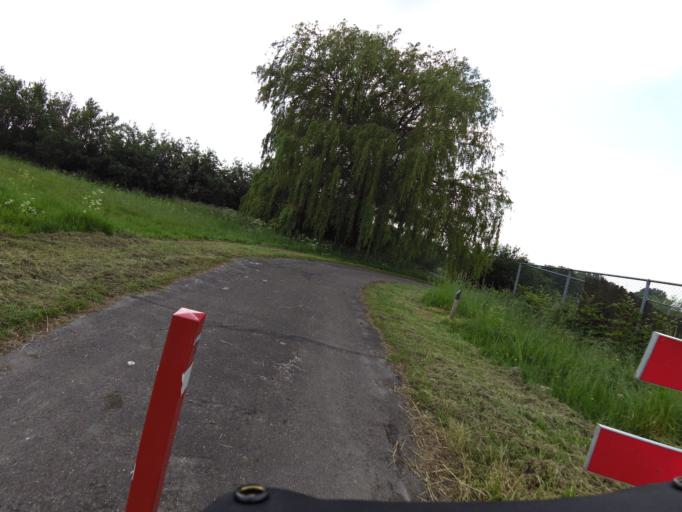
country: NL
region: South Holland
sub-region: Gemeente Spijkenisse
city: Spijkenisse
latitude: 51.8245
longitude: 4.2684
